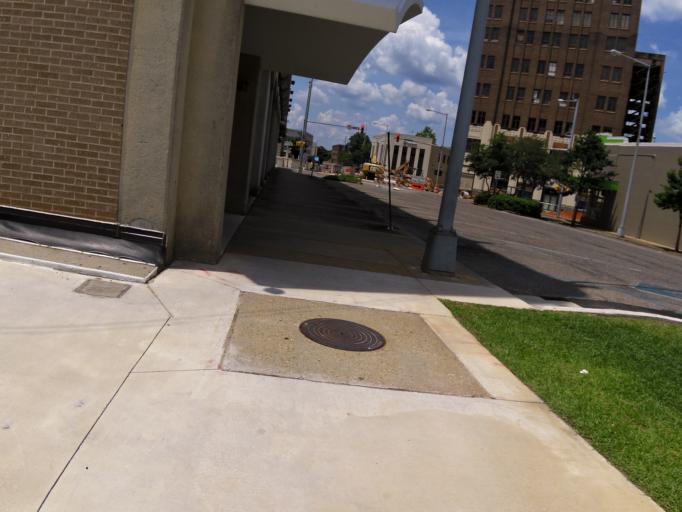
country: US
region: Mississippi
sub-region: Lauderdale County
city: Meridian
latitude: 32.3647
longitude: -88.6998
